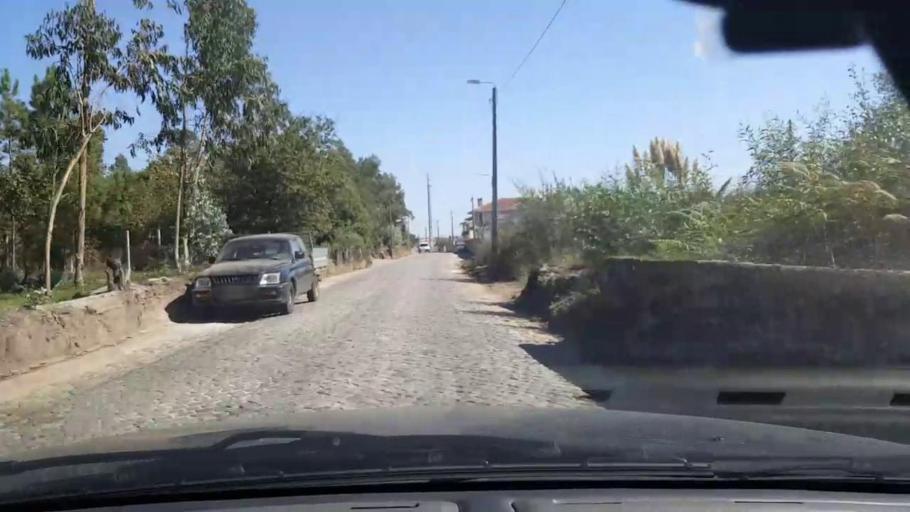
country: PT
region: Porto
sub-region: Matosinhos
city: Lavra
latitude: 41.2953
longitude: -8.7025
